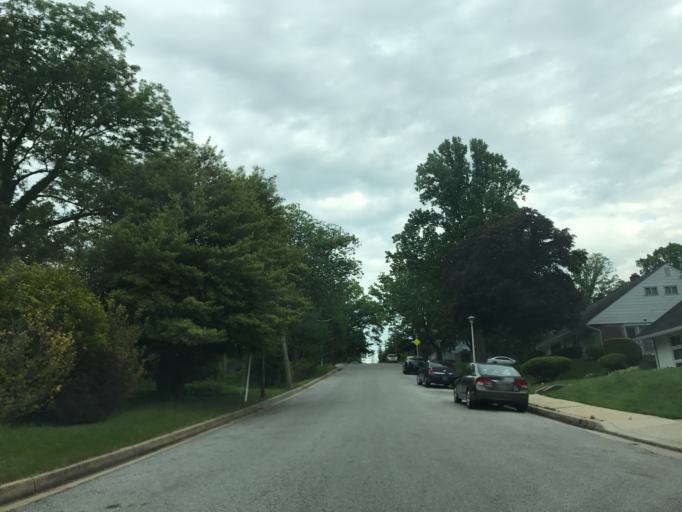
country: US
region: Maryland
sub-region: Baltimore County
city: Parkville
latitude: 39.3511
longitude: -76.5739
